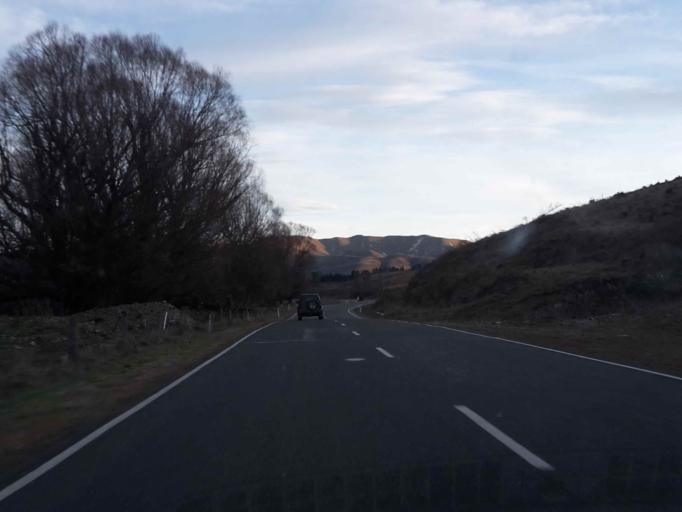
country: NZ
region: Canterbury
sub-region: Timaru District
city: Pleasant Point
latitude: -44.0684
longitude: 170.6704
